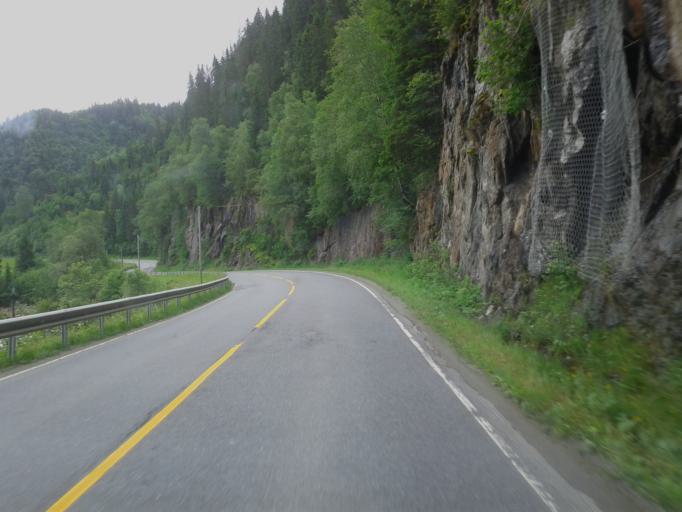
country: NO
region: Sor-Trondelag
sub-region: Midtre Gauldal
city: Storen
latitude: 62.9953
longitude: 10.4681
